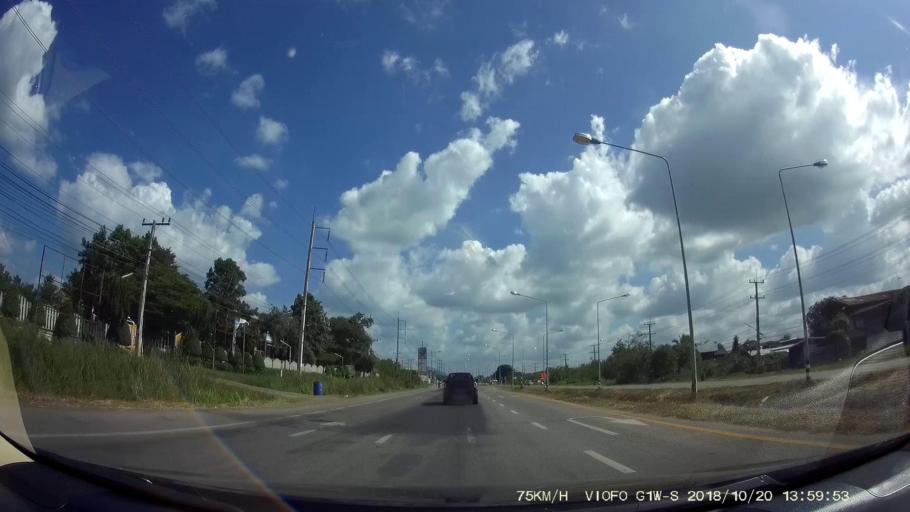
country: TH
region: Khon Kaen
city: Chum Phae
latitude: 16.5204
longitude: 102.1157
